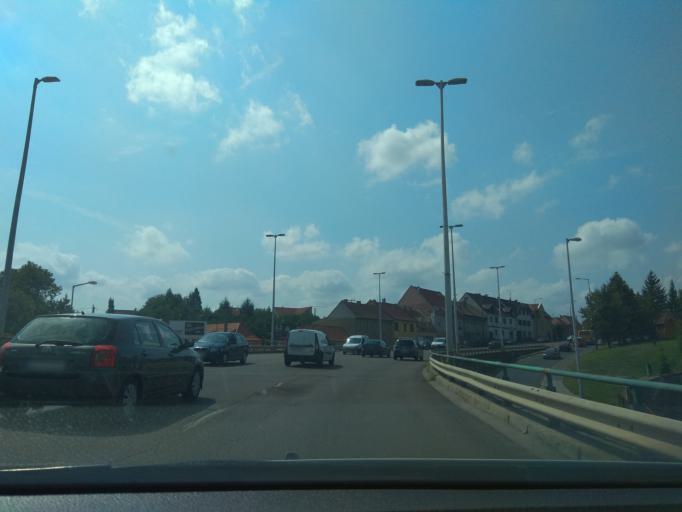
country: HU
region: Heves
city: Eger
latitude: 47.9088
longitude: 20.3702
